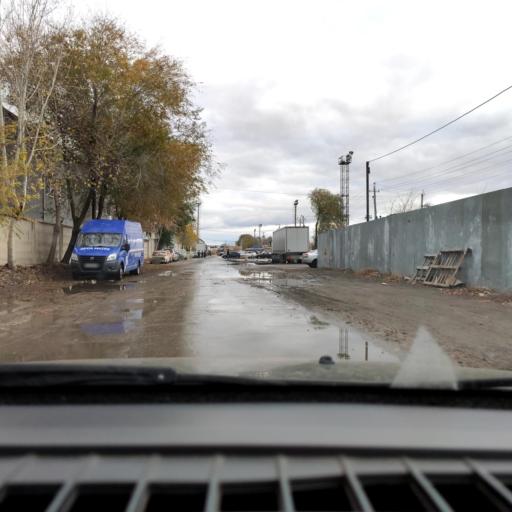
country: RU
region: Samara
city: Tol'yatti
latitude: 53.5721
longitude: 49.2829
